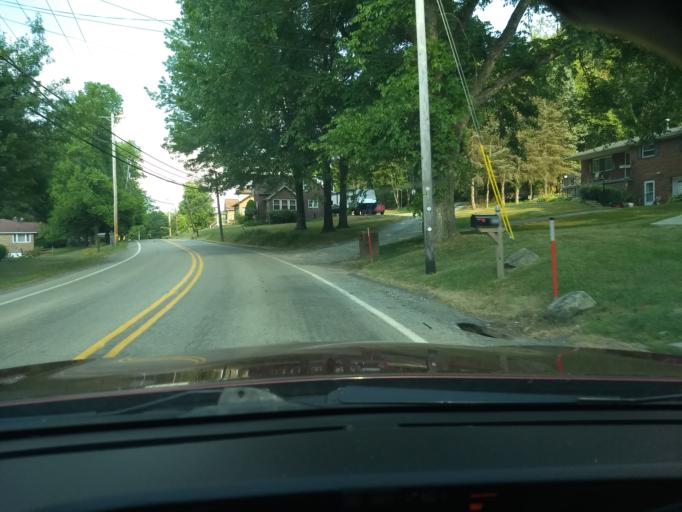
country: US
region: Pennsylvania
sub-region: Allegheny County
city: Plum
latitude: 40.4774
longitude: -79.7483
